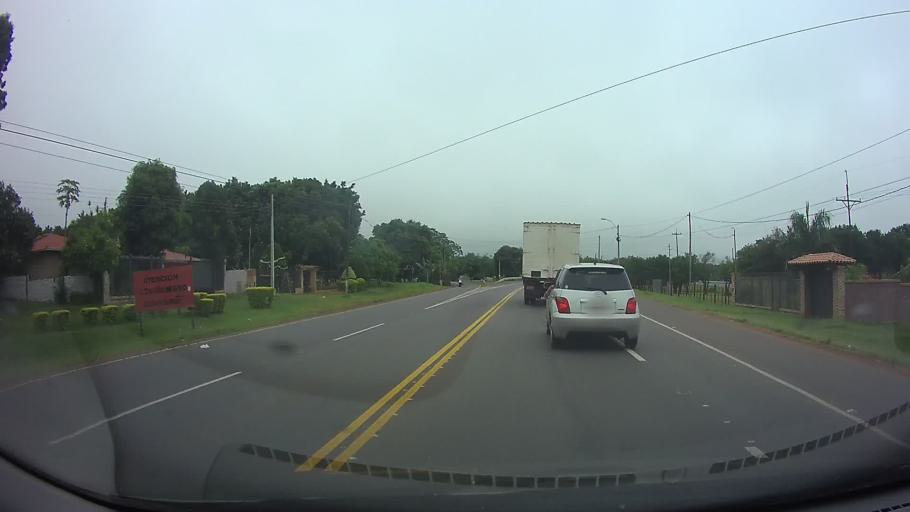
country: PY
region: Paraguari
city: Paraguari
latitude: -25.6030
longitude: -57.1892
